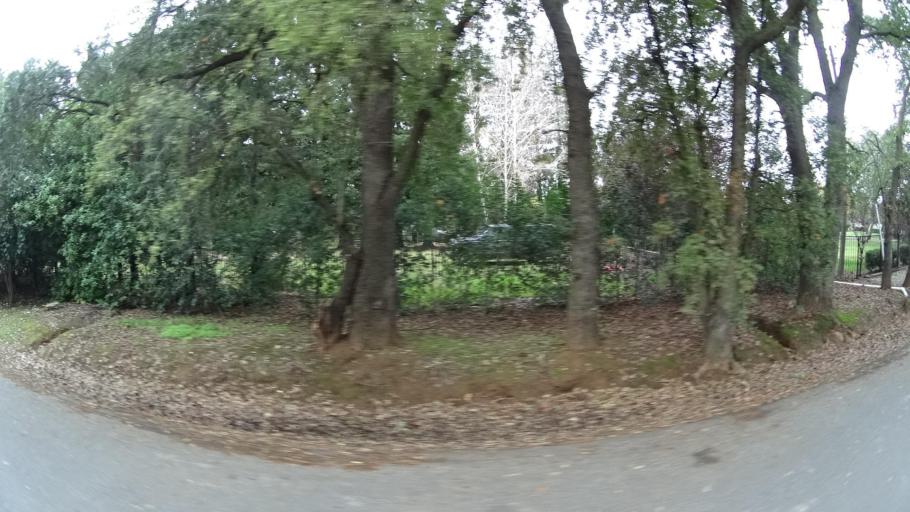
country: US
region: California
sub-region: Sacramento County
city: Wilton
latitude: 38.4408
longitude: -121.3069
